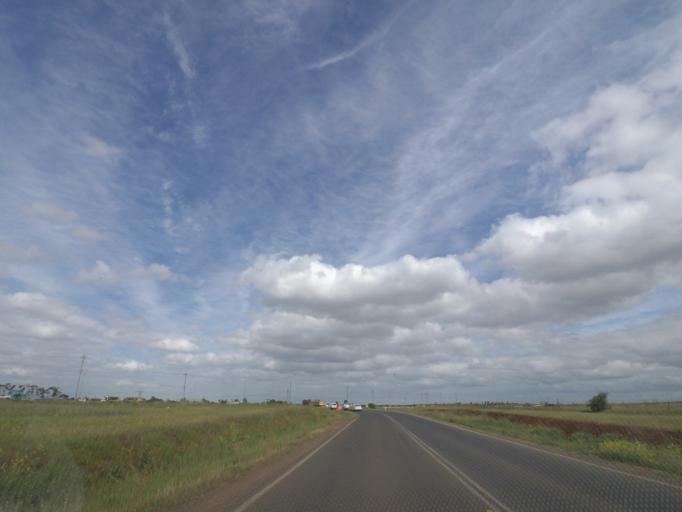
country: AU
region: Victoria
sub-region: Melton
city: Caroline Springs
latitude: -37.7520
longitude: 144.7019
